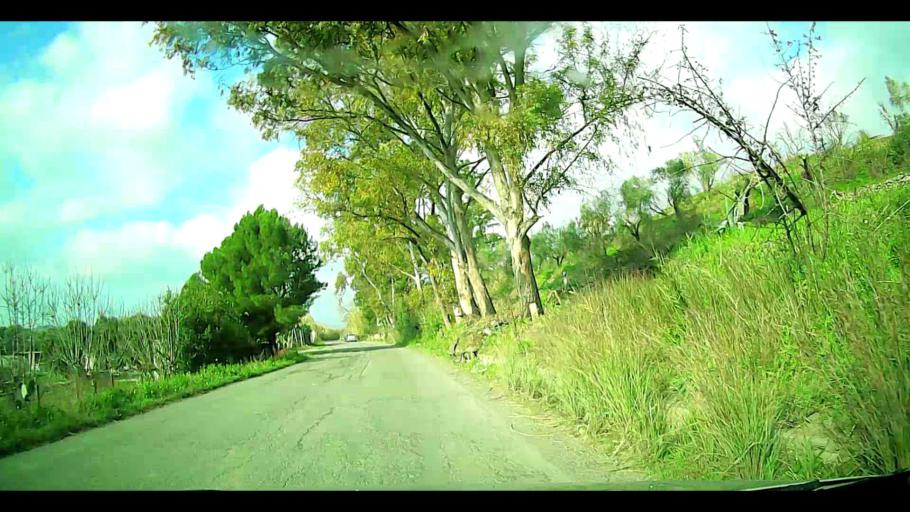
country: IT
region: Calabria
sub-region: Provincia di Crotone
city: Rocca di Neto
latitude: 39.1800
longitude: 17.0324
